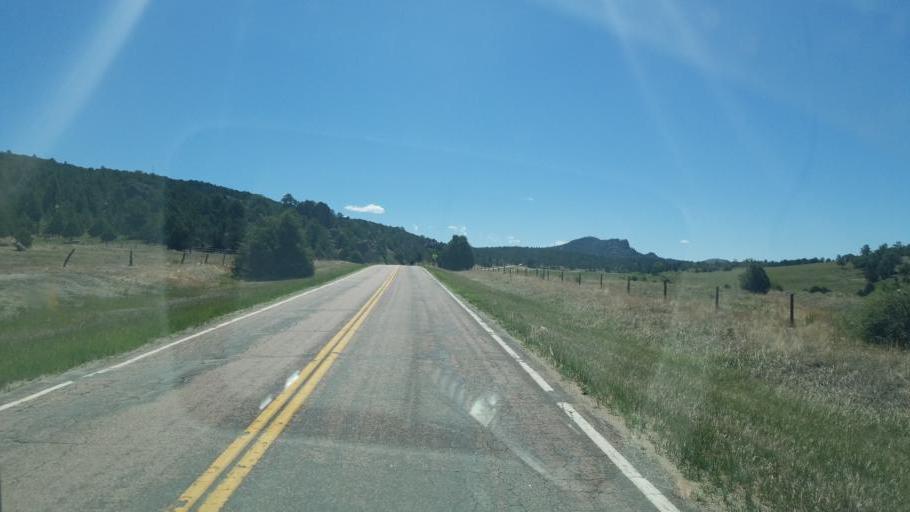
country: US
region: Colorado
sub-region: Custer County
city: Westcliffe
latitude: 38.2506
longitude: -105.5798
